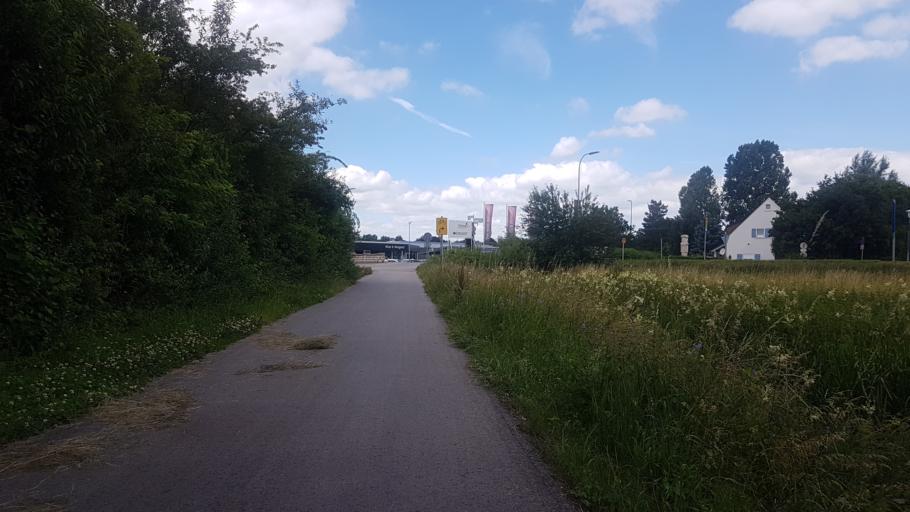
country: DE
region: Bavaria
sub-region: Regierungsbezirk Mittelfranken
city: Gunzenhausen
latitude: 49.1138
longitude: 10.7501
